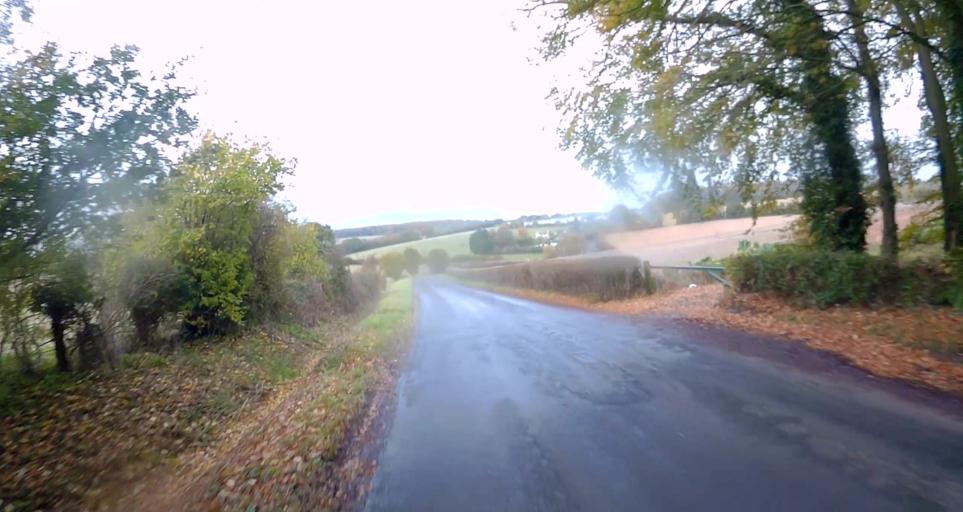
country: GB
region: England
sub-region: Hampshire
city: Four Marks
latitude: 51.1667
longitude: -1.0452
